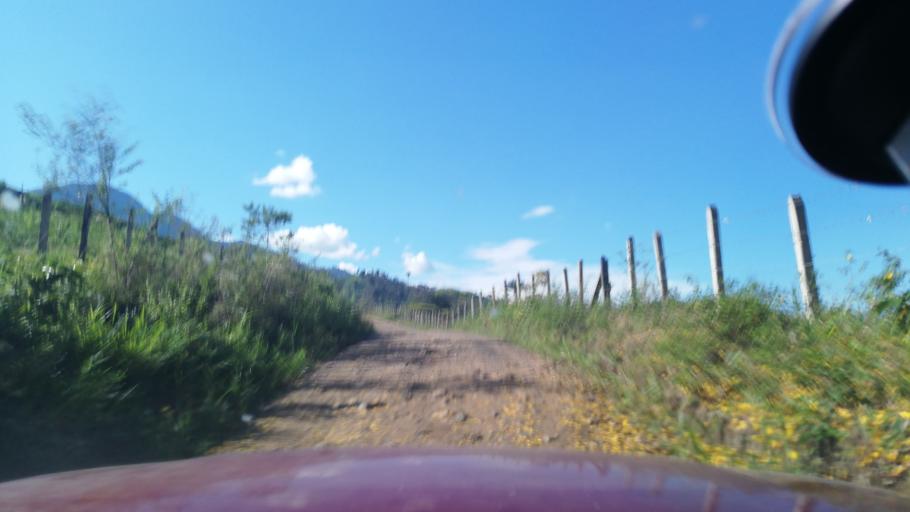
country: CO
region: Cundinamarca
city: Quipile
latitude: 4.7763
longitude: -74.6177
